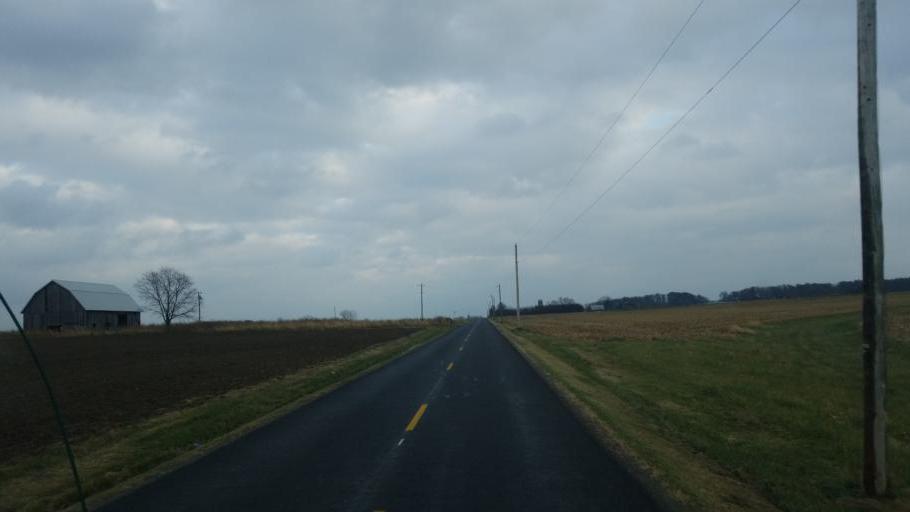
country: US
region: Ohio
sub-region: Mercer County
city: Fort Recovery
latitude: 40.5090
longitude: -84.7309
